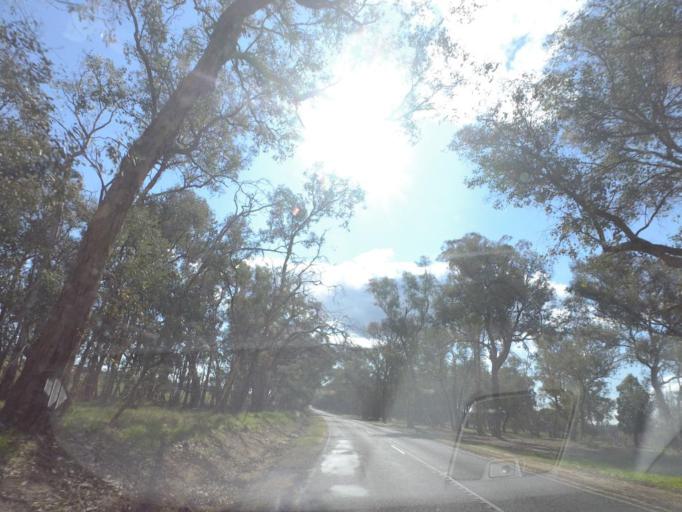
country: AU
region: New South Wales
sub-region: Corowa Shire
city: Howlong
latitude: -36.2304
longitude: 146.6310
